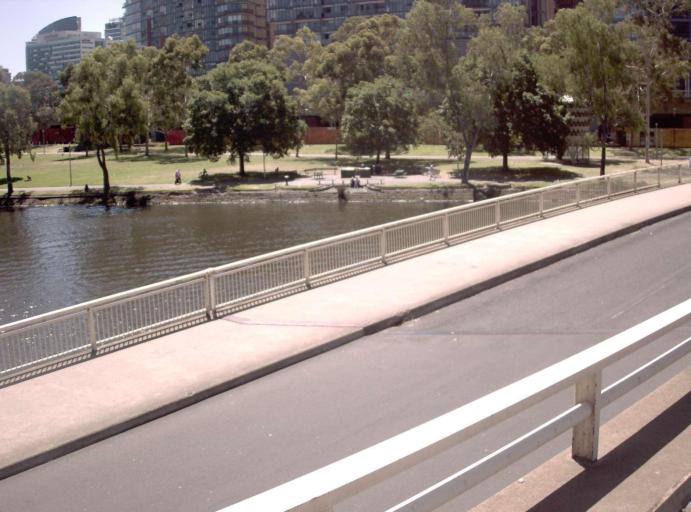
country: AU
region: Victoria
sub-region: Melbourne
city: Southbank
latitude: -37.8222
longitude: 144.9581
